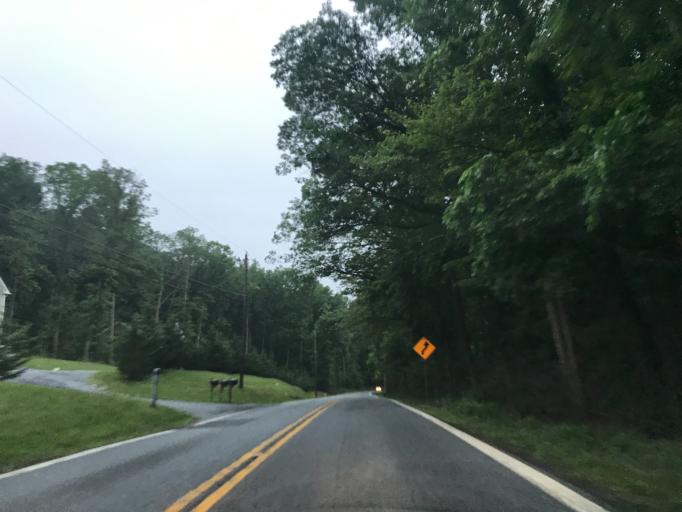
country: US
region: Maryland
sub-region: Frederick County
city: Linganore
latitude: 39.4751
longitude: -77.2449
